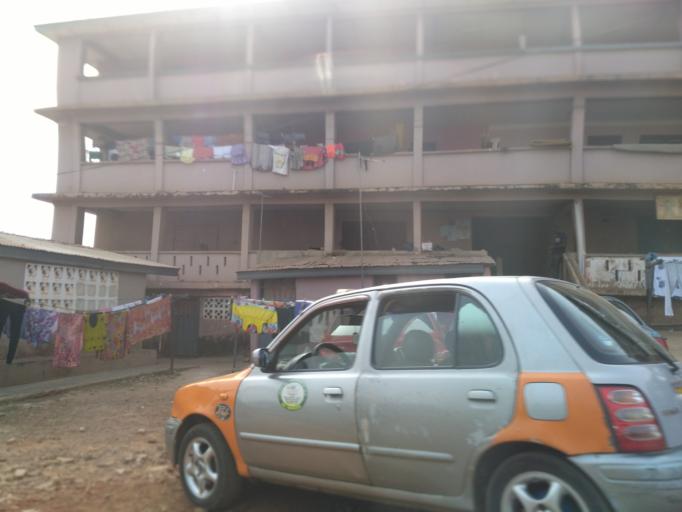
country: GH
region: Ashanti
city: Kumasi
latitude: 6.7036
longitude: -1.6036
